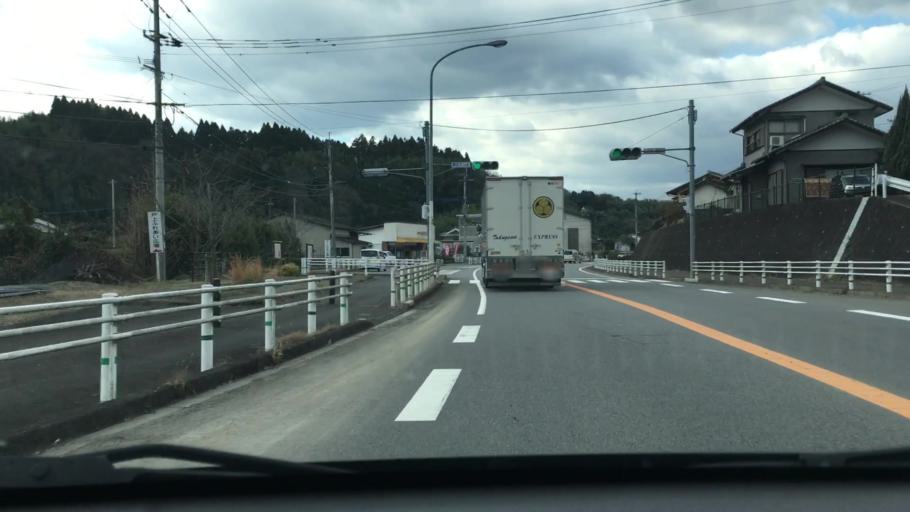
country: JP
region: Oita
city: Usuki
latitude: 33.0651
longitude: 131.6603
